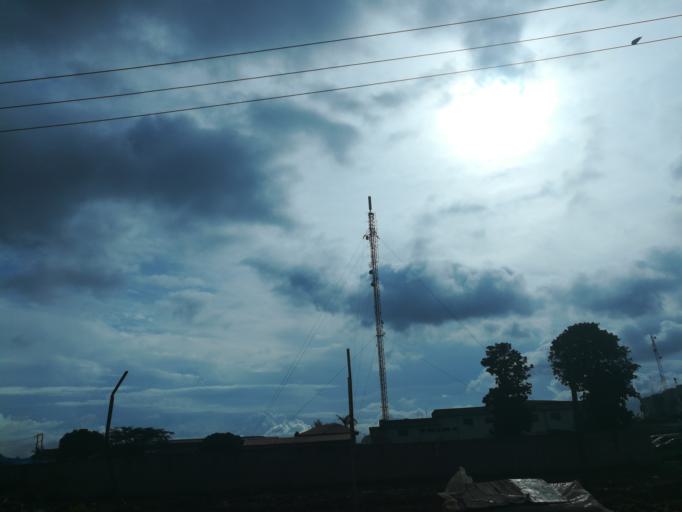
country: NG
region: Lagos
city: Ikeja
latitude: 6.6170
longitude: 3.3560
